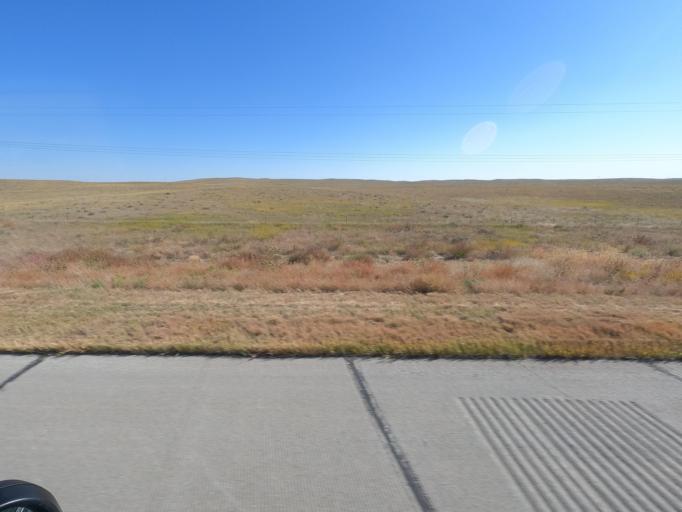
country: US
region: Nebraska
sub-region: Cheyenne County
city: Sidney
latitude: 40.7953
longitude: -102.8797
